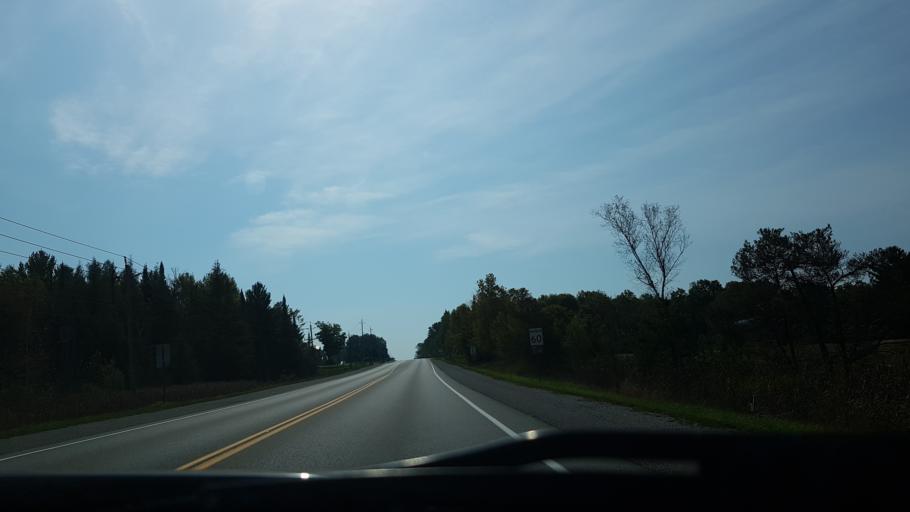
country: CA
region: Ontario
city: Orillia
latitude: 44.7302
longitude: -79.2886
